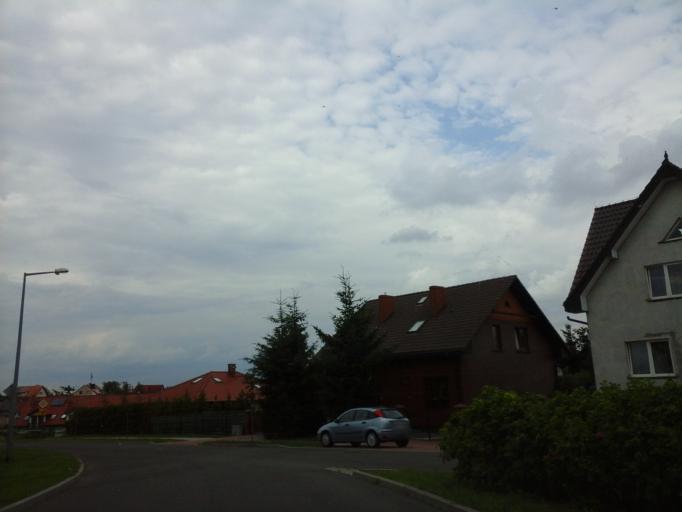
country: PL
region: West Pomeranian Voivodeship
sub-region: Powiat choszczenski
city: Choszczno
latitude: 53.1761
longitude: 15.4084
